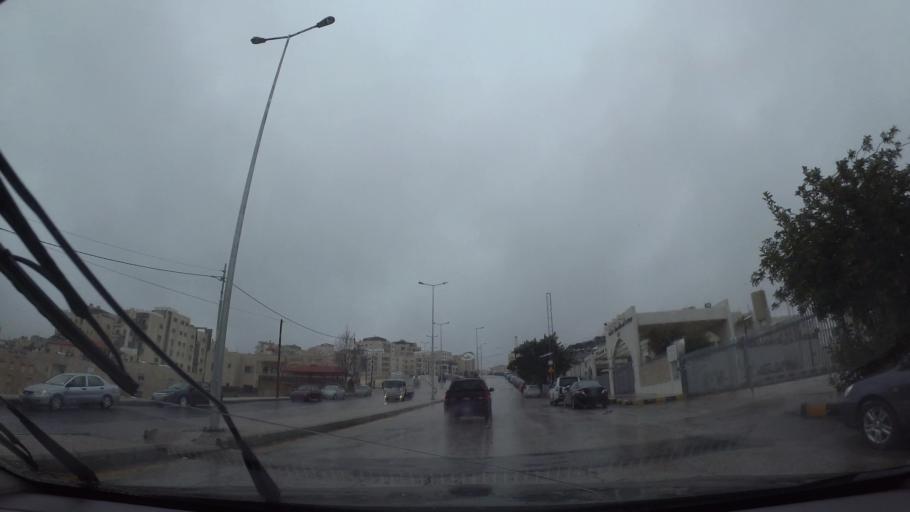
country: JO
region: Amman
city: Al Jubayhah
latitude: 32.0159
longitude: 35.8917
